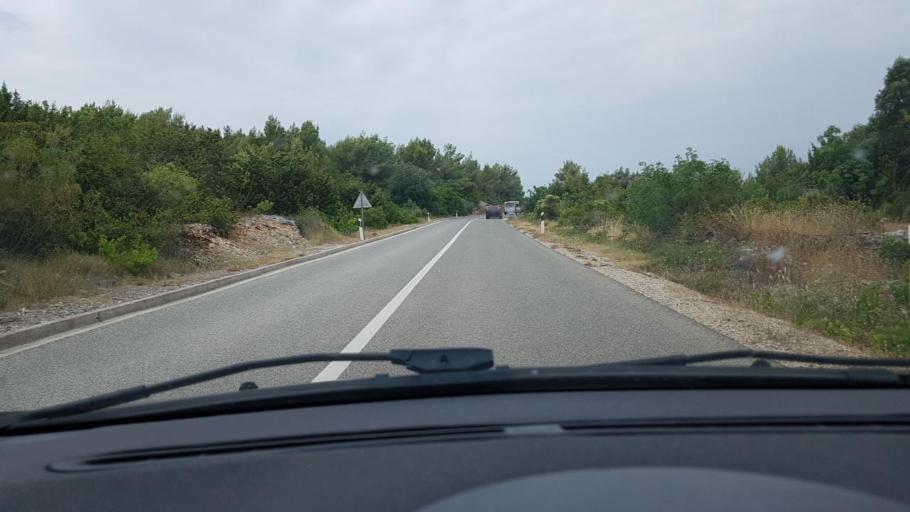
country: HR
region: Dubrovacko-Neretvanska
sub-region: Grad Korcula
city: Zrnovo
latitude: 42.9371
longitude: 17.0802
